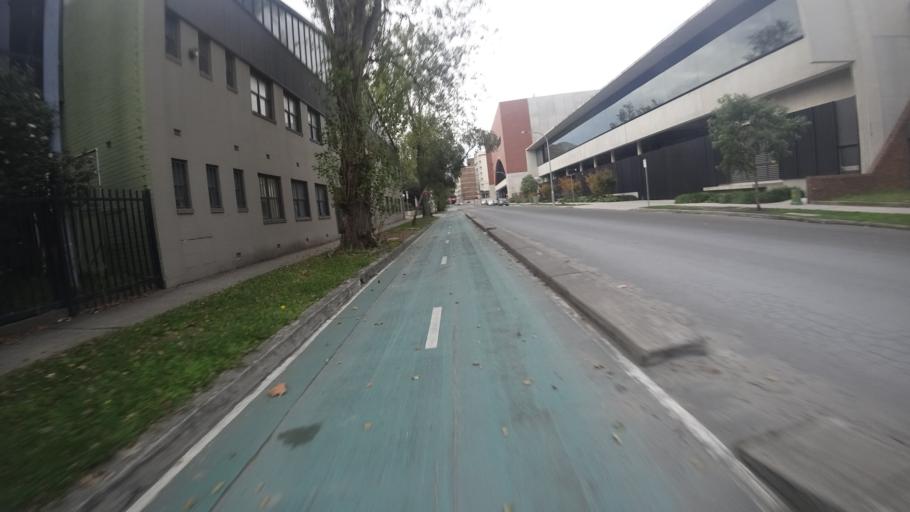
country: AU
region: New South Wales
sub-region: City of Sydney
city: Alexandria
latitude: -33.9048
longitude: 151.1996
